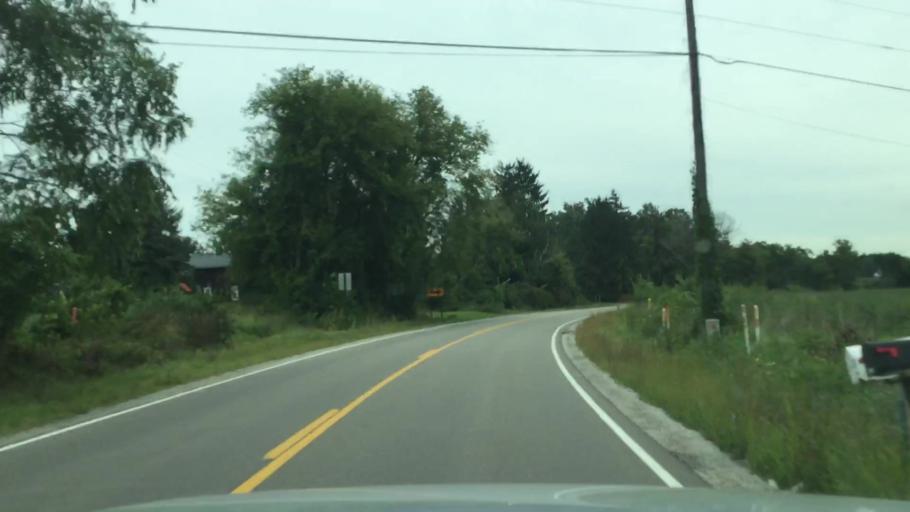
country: US
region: Michigan
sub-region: Washtenaw County
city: Ypsilanti
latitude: 42.1944
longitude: -83.6317
